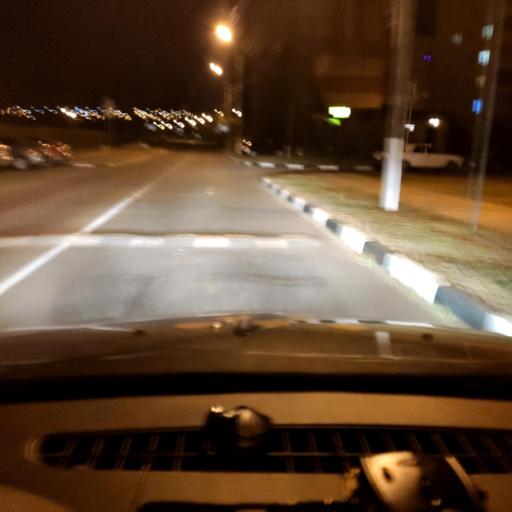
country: RU
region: Belgorod
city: Mayskiy
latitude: 50.5199
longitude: 36.4545
